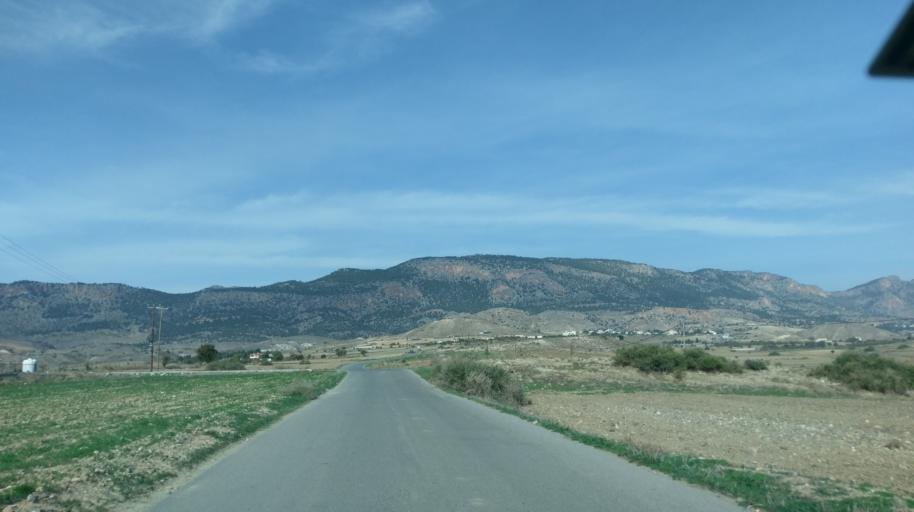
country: CY
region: Keryneia
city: Lapithos
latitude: 35.2724
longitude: 33.2250
